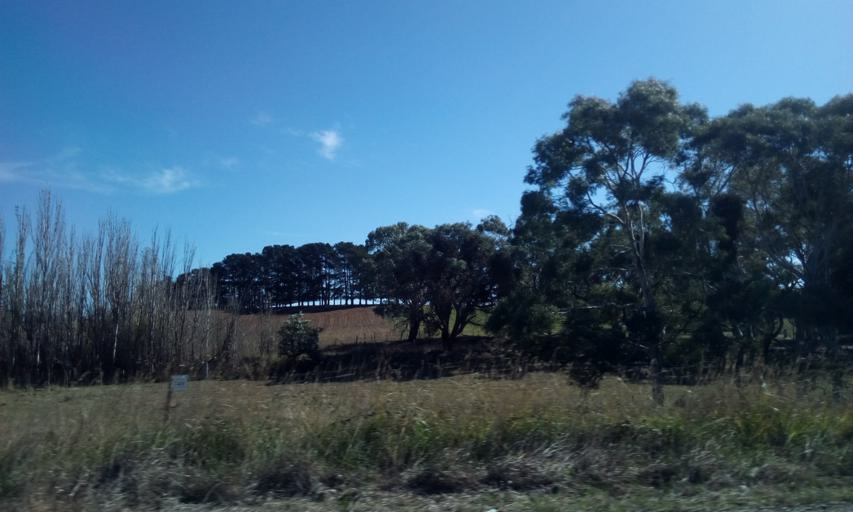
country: AU
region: New South Wales
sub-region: Yass Valley
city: Gundaroo
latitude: -35.1384
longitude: 149.3374
